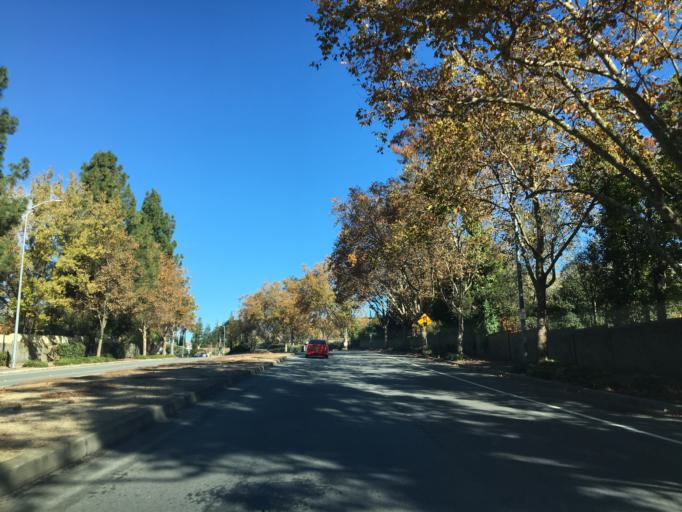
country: US
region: California
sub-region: Santa Clara County
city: Milpitas
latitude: 37.4985
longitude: -121.9199
